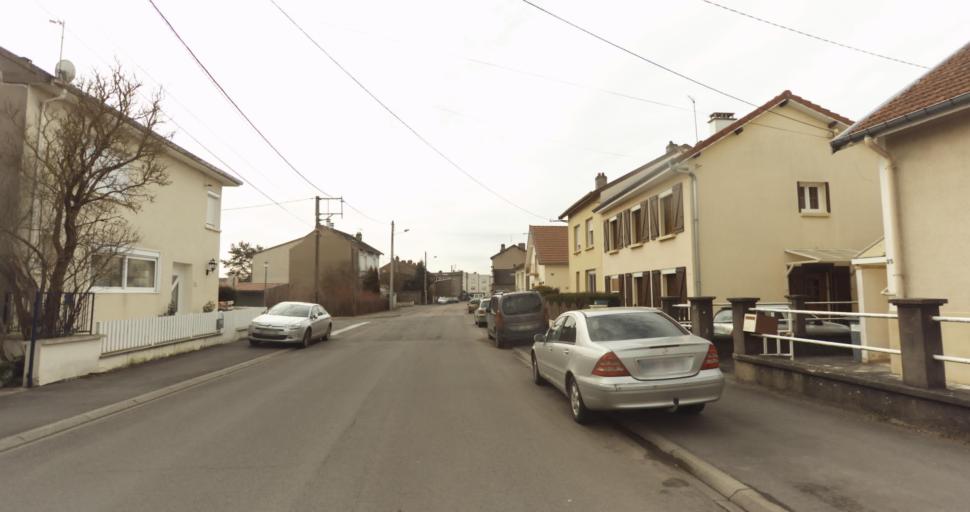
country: FR
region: Lorraine
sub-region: Departement de Meurthe-et-Moselle
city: Jarny
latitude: 49.1611
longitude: 5.8770
